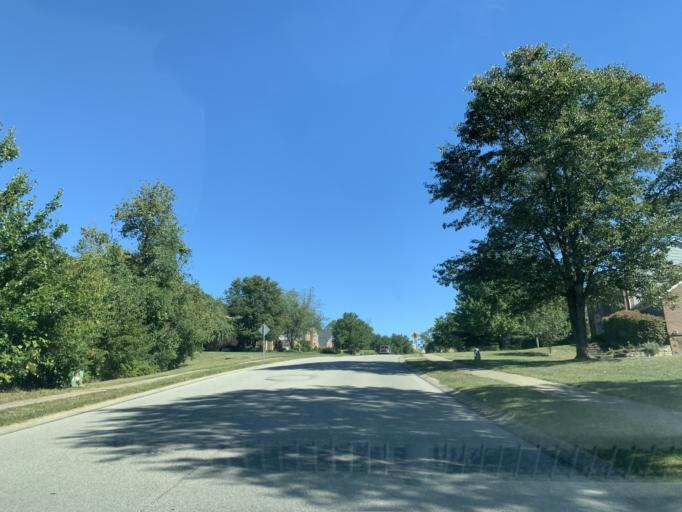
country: US
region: Kentucky
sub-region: Boone County
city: Francisville
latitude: 39.1013
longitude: -84.7262
